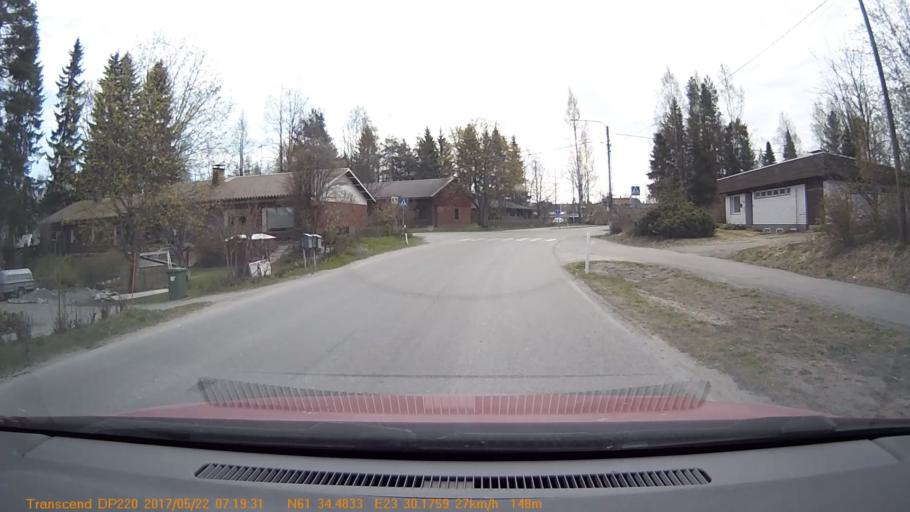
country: FI
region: Pirkanmaa
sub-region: Tampere
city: Yloejaervi
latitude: 61.5747
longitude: 23.5028
